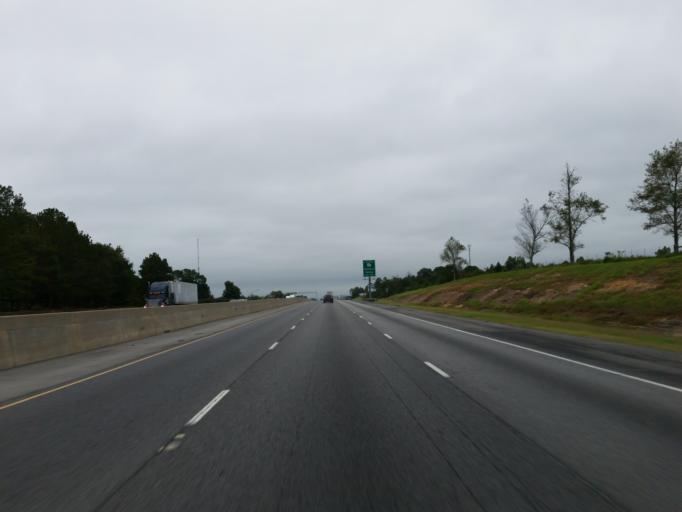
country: US
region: Georgia
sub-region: Turner County
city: Ashburn
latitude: 31.7518
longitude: -83.6641
